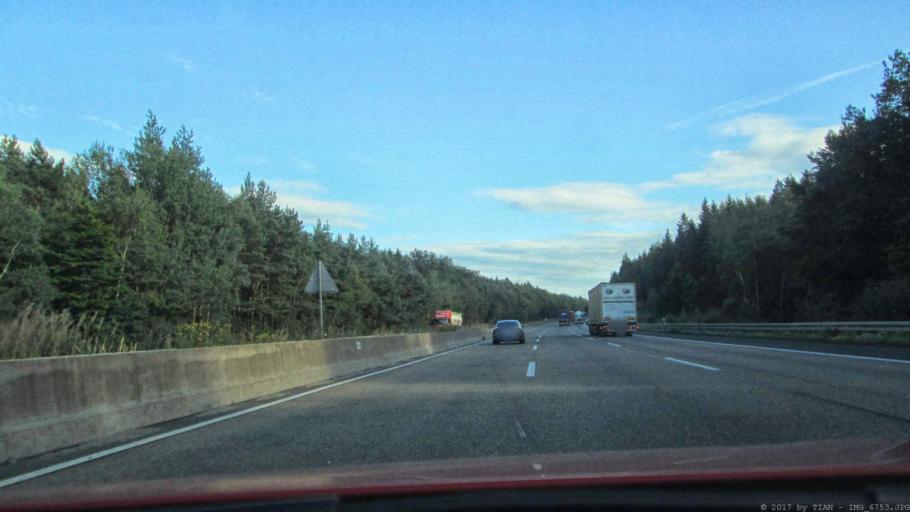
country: DE
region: Hesse
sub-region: Regierungsbezirk Kassel
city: Burghaun
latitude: 50.6968
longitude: 9.6815
